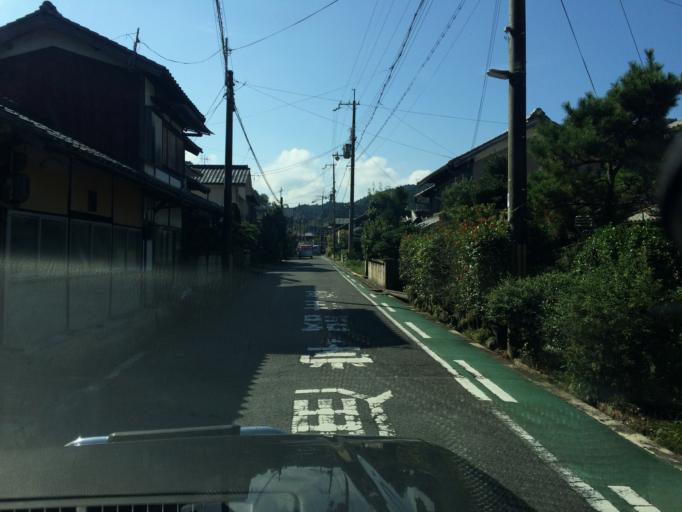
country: JP
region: Nara
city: Nara-shi
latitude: 34.7360
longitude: 135.9522
